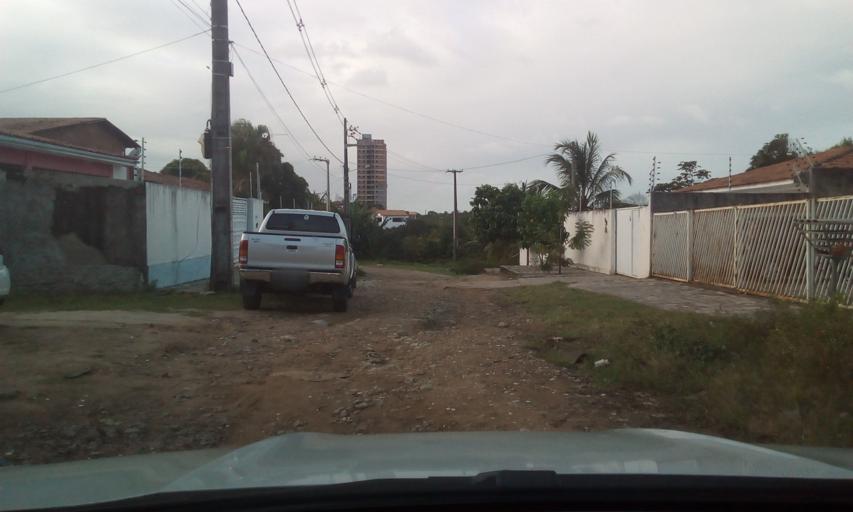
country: BR
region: Paraiba
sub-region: Joao Pessoa
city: Joao Pessoa
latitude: -7.1594
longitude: -34.8239
